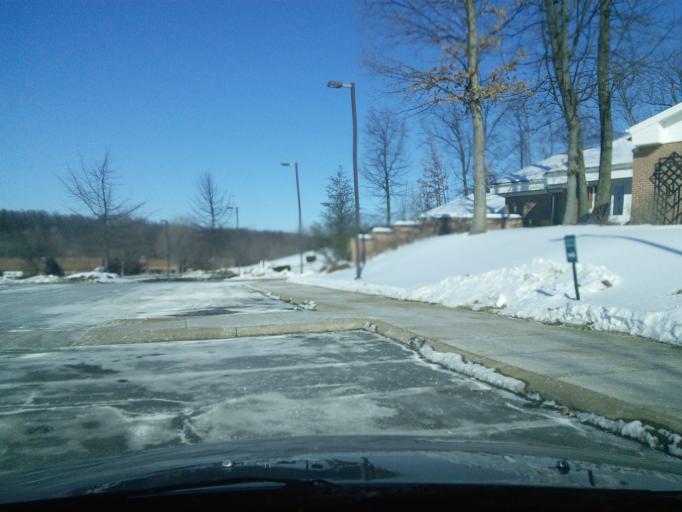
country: US
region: Pennsylvania
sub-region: Centre County
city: Park Forest Village
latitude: 40.8124
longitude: -77.9205
